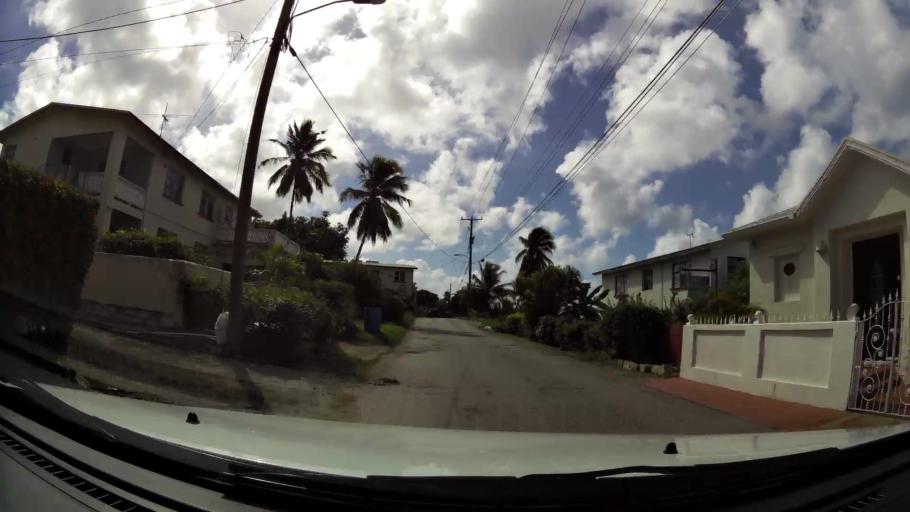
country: BB
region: Saint Lucy
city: Checker Hall
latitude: 13.2759
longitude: -59.6469
